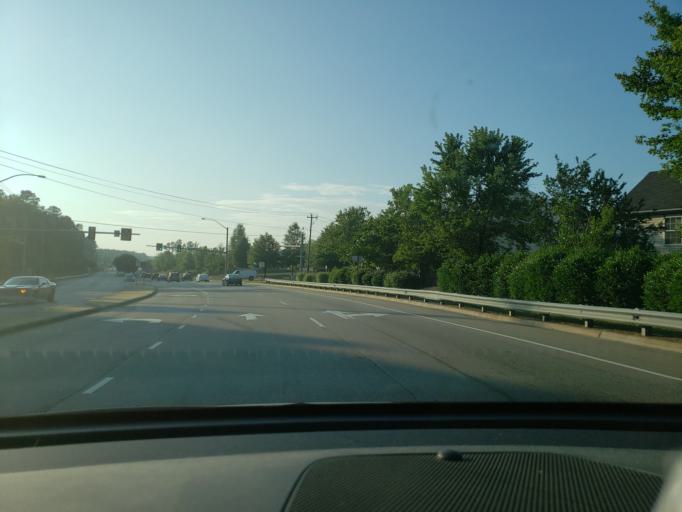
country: US
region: North Carolina
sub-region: Durham County
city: Durham
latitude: 35.9454
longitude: -78.9211
